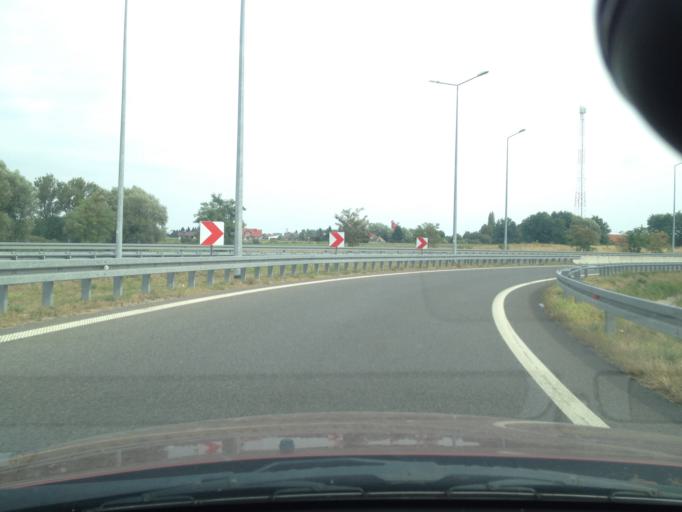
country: PL
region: West Pomeranian Voivodeship
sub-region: Powiat pyrzycki
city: Lipiany
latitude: 52.9532
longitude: 14.9477
